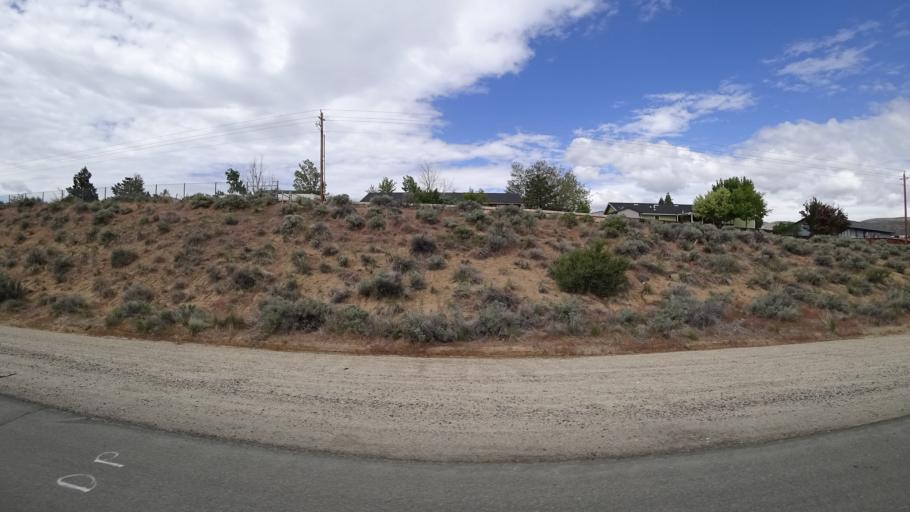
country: US
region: Nevada
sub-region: Douglas County
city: Indian Hills
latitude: 39.0888
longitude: -119.7757
